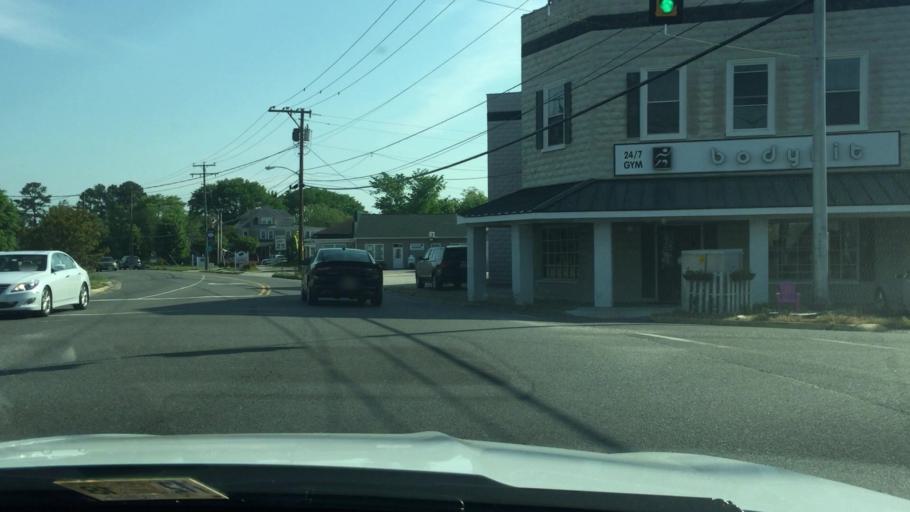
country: US
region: Virginia
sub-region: Lancaster County
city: Kilmarnock
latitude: 37.6484
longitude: -76.3893
